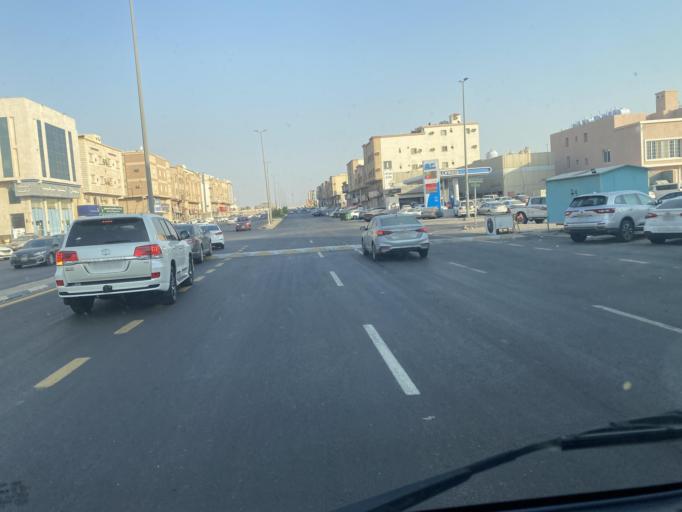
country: SA
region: Eastern Province
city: Dhahran
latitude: 26.3550
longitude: 50.0475
